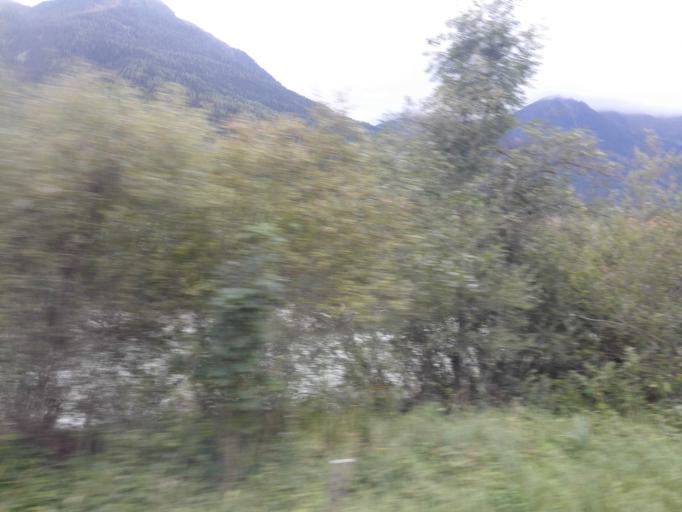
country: AT
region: Salzburg
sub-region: Politischer Bezirk Zell am See
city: Bramberg am Wildkogel
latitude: 47.2667
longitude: 12.3364
